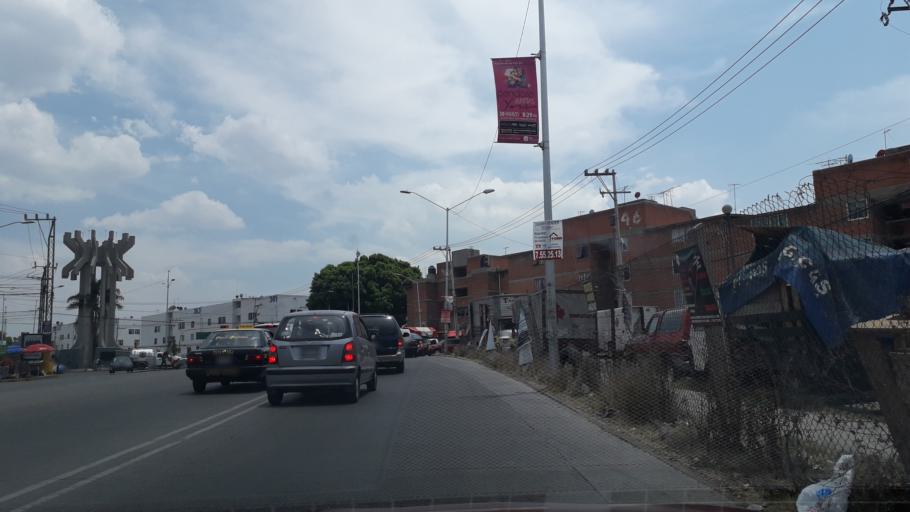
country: MX
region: Puebla
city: Puebla
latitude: 19.0103
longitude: -98.1884
